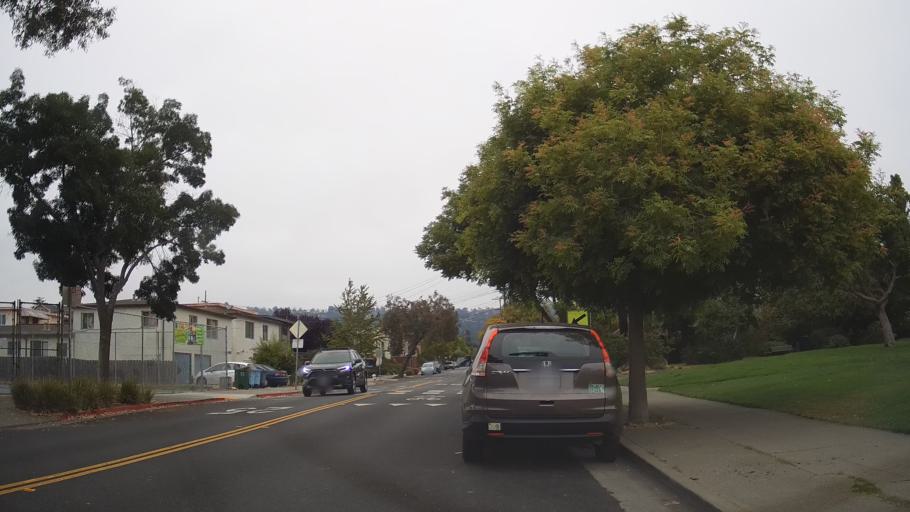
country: US
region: California
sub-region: Alameda County
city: Albany
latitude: 37.8770
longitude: -122.2883
